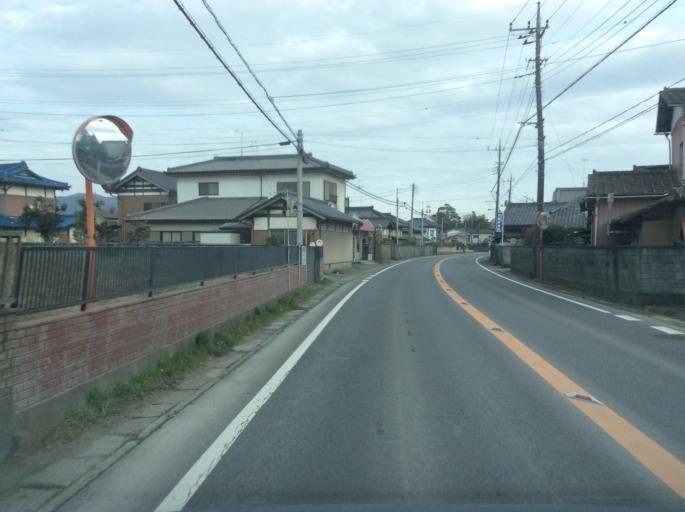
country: JP
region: Ibaraki
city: Tsukuba
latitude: 36.1817
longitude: 140.0656
